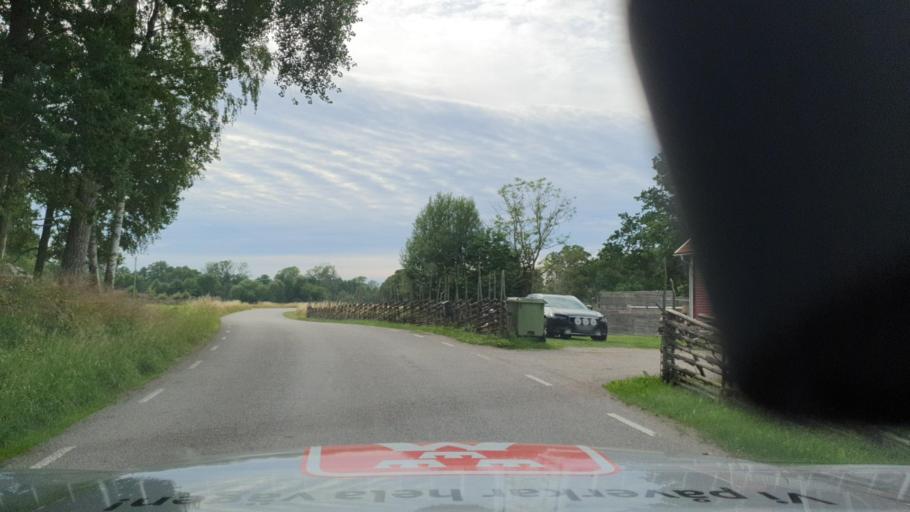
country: SE
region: Kalmar
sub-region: Kalmar Kommun
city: Ljungbyholm
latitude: 56.5878
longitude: 16.0927
